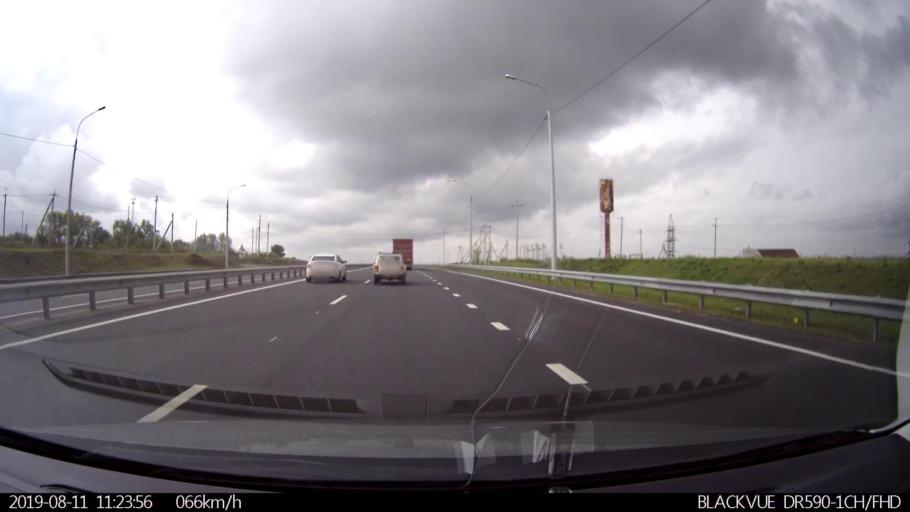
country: RU
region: Ulyanovsk
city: Krasnyy Gulyay
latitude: 54.1317
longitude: 48.2474
